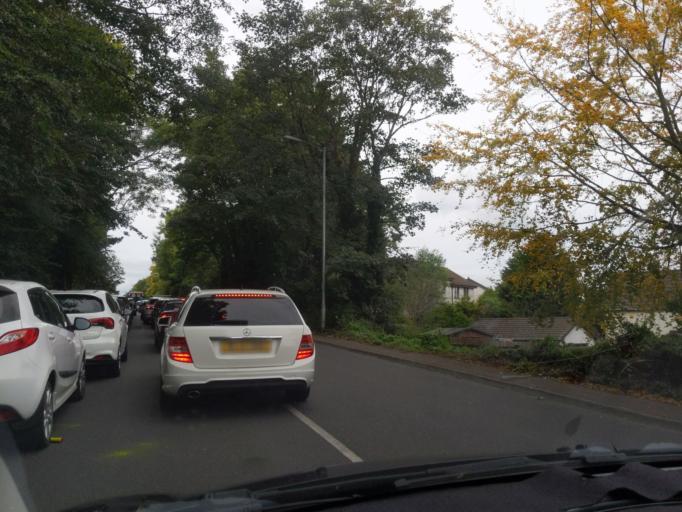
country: GB
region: England
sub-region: Cornwall
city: St Austell
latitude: 50.3374
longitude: -4.7660
